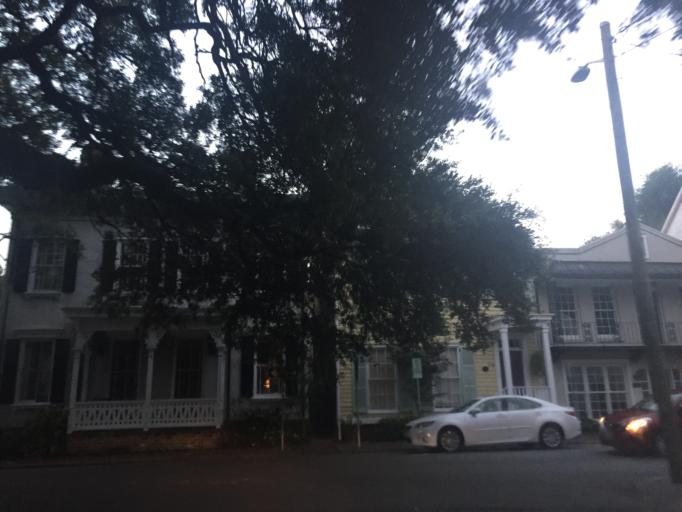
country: US
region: Georgia
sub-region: Chatham County
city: Savannah
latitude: 32.0782
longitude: -81.0857
